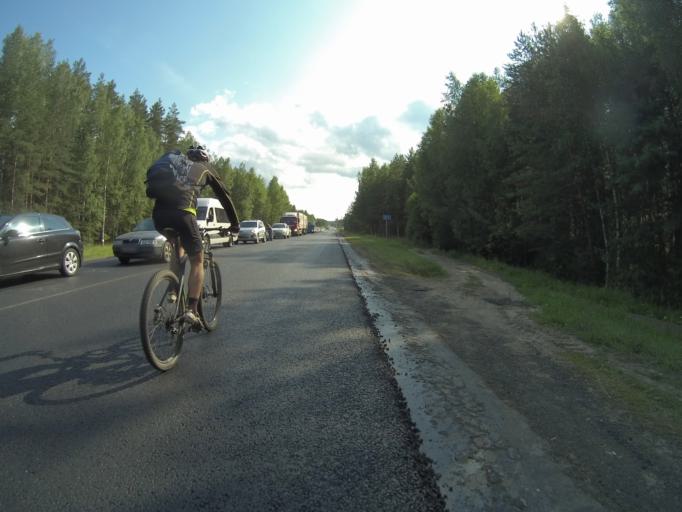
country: RU
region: Ivanovo
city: Novoye Leushino
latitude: 56.6945
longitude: 40.6249
